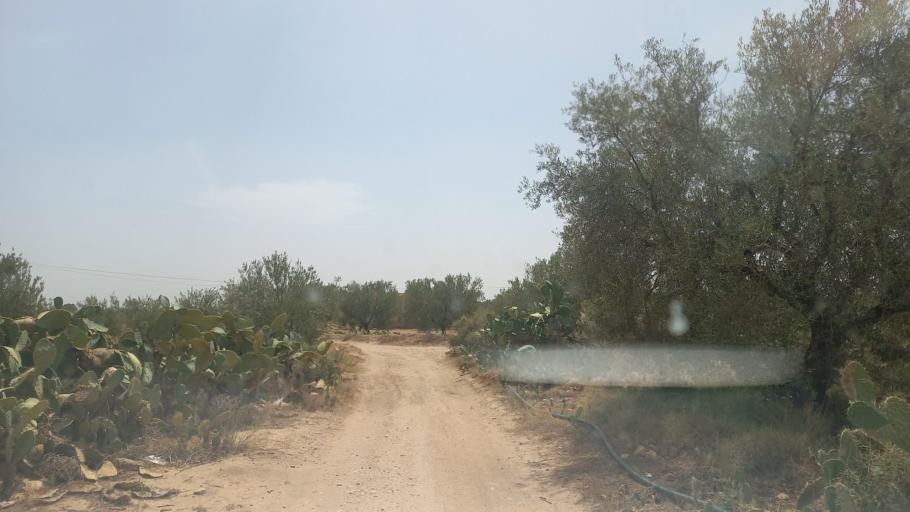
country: TN
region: Al Qasrayn
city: Kasserine
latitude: 35.2558
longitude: 9.0097
